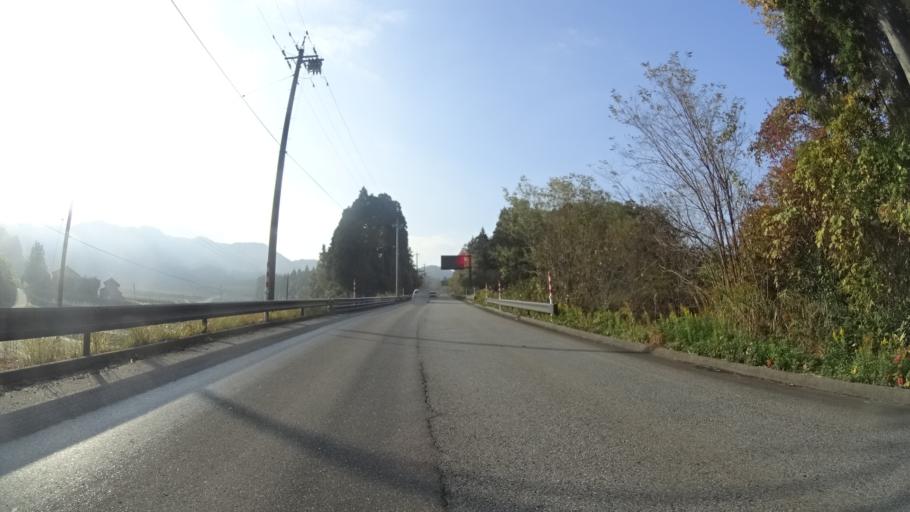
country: JP
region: Ishikawa
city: Nanao
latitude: 37.0268
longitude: 136.9856
